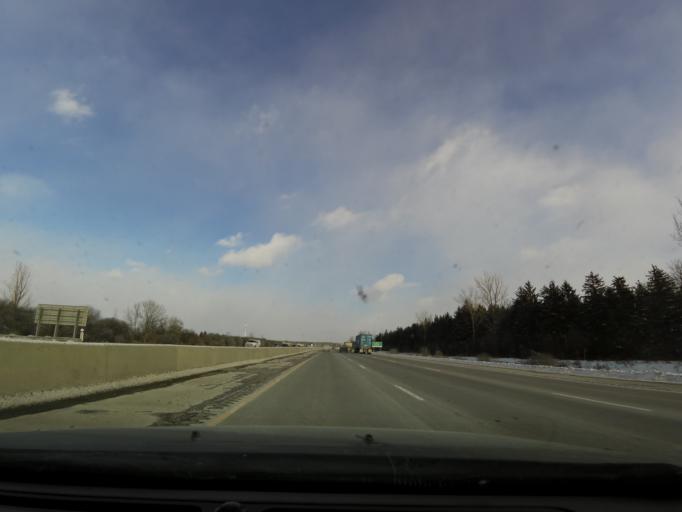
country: CA
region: Ontario
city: Cambridge
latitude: 43.4295
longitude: -80.2591
